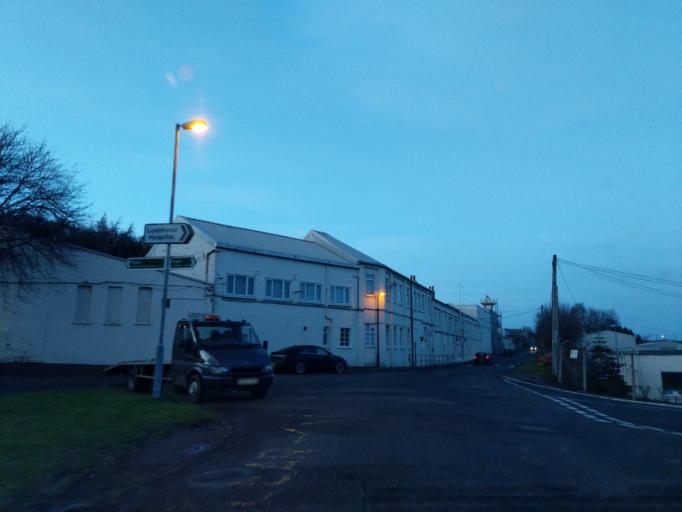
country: GB
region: Scotland
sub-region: Midlothian
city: Loanhead
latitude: 55.8802
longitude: -3.1426
